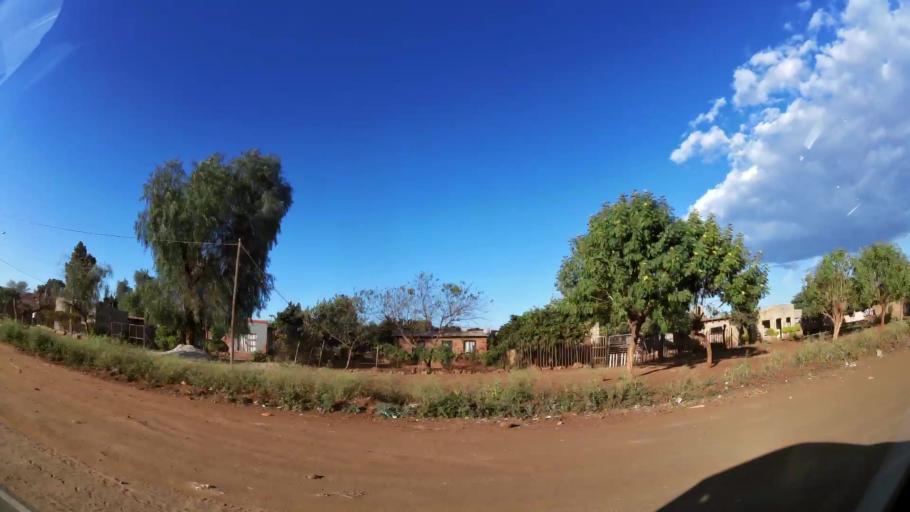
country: ZA
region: Limpopo
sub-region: Waterberg District Municipality
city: Mokopane
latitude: -24.1682
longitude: 28.9847
